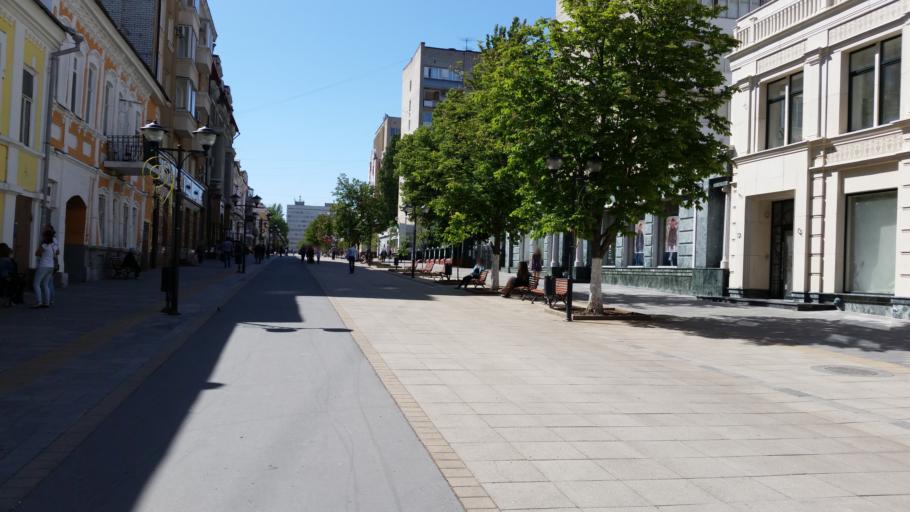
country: RU
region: Saratov
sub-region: Saratovskiy Rayon
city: Saratov
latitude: 51.5286
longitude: 46.0424
